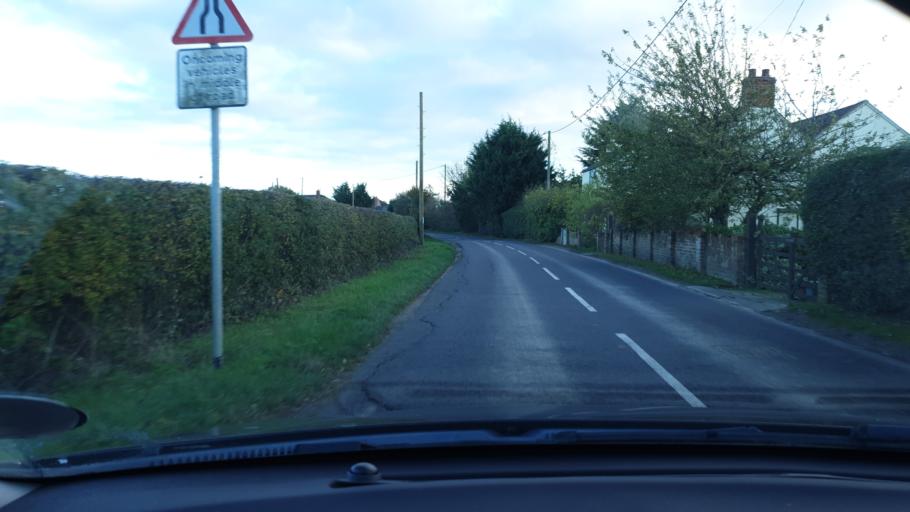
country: GB
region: England
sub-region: Essex
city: Little Clacton
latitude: 51.8975
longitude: 1.1458
